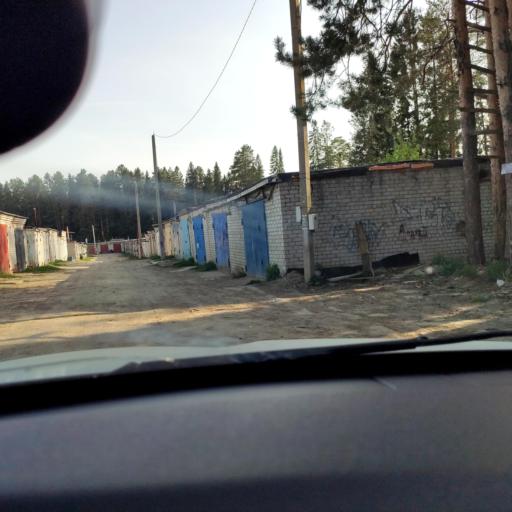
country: RU
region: Perm
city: Polazna
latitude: 58.2958
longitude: 56.3875
